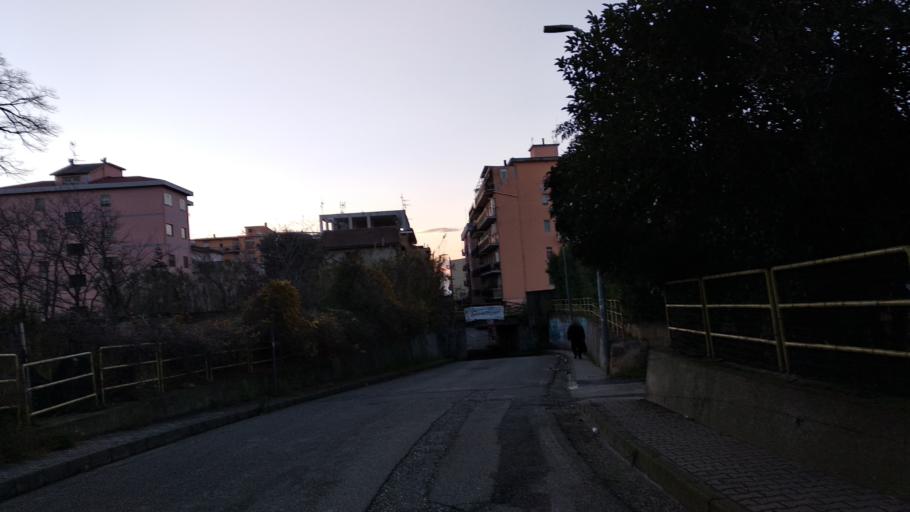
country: IT
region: Calabria
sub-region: Provincia di Catanzaro
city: Barone
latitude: 38.8287
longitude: 16.6252
